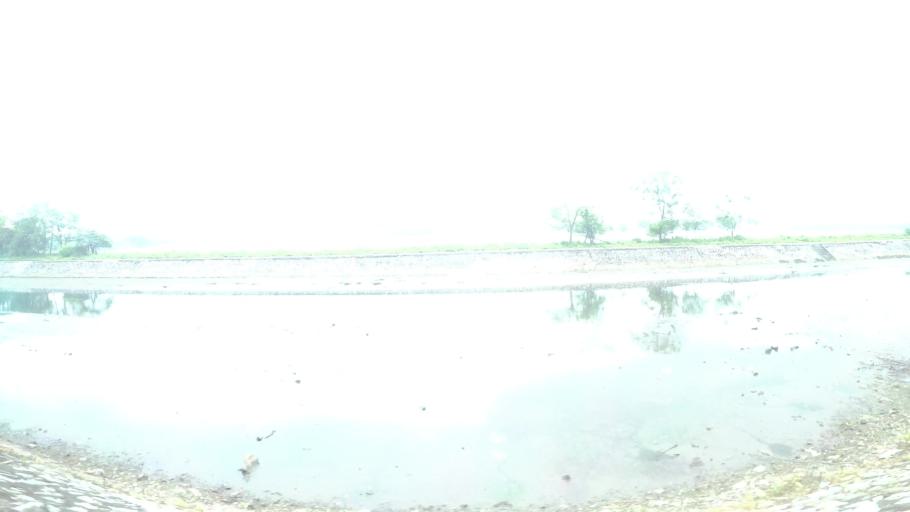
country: VN
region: Ha Noi
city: Van Dien
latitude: 20.9727
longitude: 105.8542
